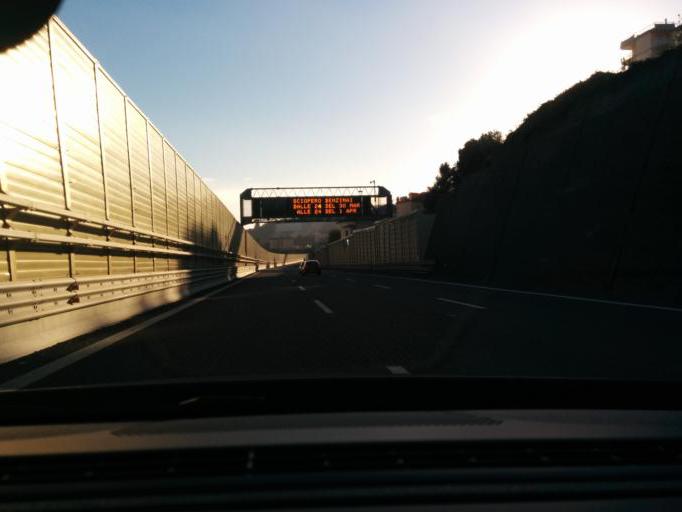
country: IT
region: Liguria
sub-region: Provincia di Genova
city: Arenzano
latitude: 44.4062
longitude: 8.6763
